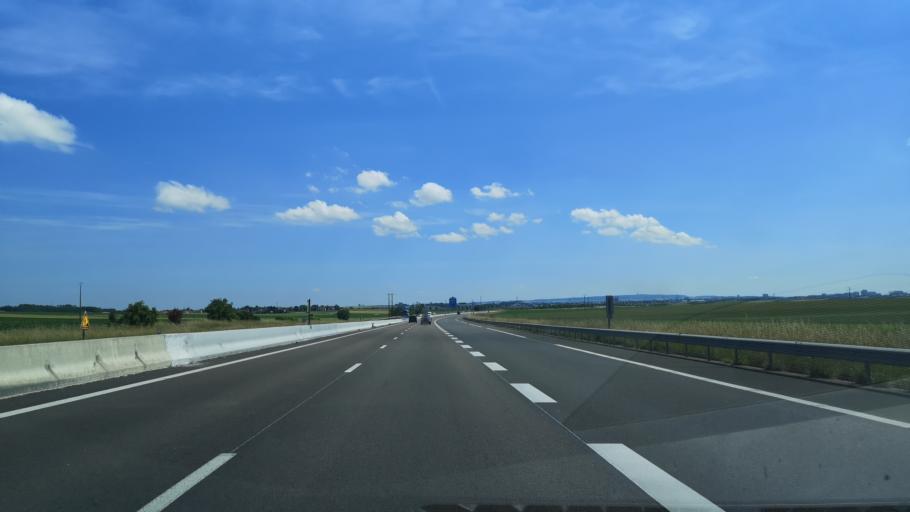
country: FR
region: Champagne-Ardenne
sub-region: Departement de la Marne
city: Gueux
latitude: 49.2459
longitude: 3.9337
